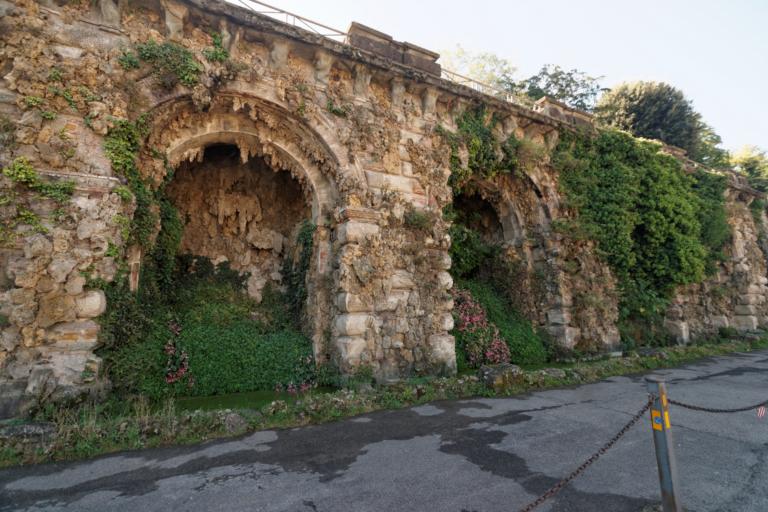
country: IT
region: Tuscany
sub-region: Province of Florence
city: Florence
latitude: 43.7641
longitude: 11.2649
